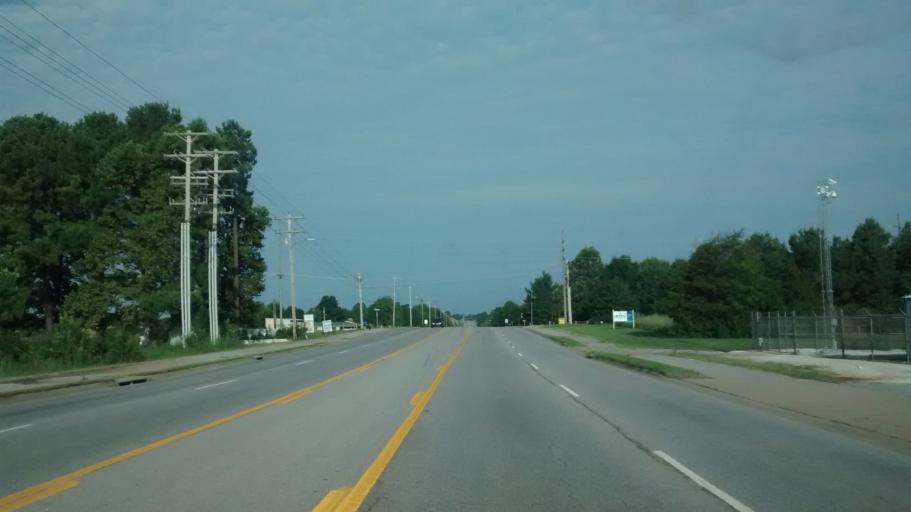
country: US
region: Arkansas
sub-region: Washington County
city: Farmington
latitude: 36.0790
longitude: -94.2290
